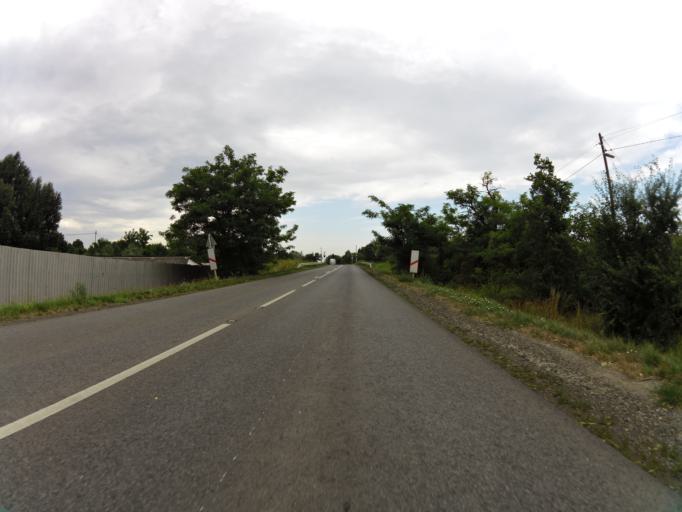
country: HU
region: Csongrad
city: Szeged
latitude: 46.2829
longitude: 20.1433
